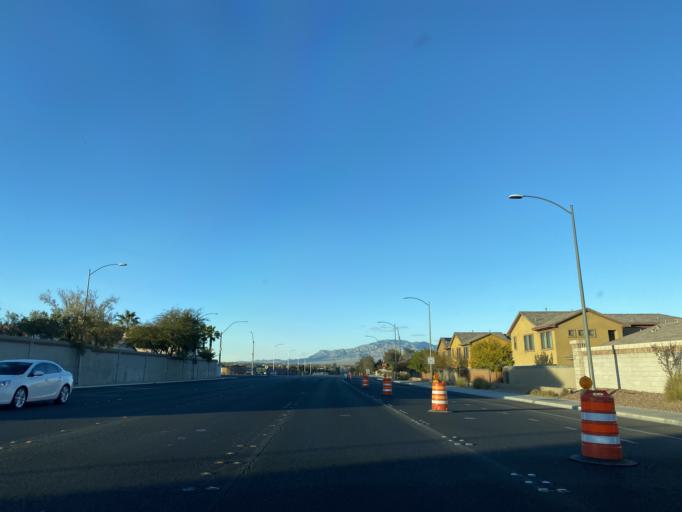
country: US
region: Nevada
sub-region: Clark County
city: Summerlin South
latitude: 36.2324
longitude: -115.2976
